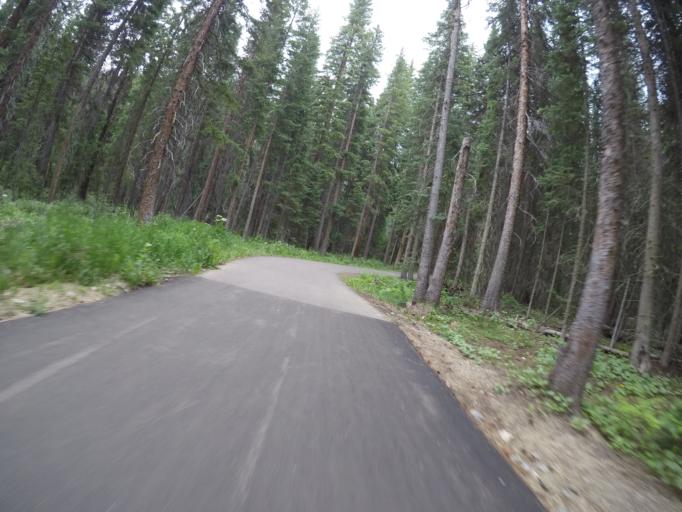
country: US
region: Colorado
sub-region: Grand County
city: Fraser
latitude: 39.9072
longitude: -105.7796
